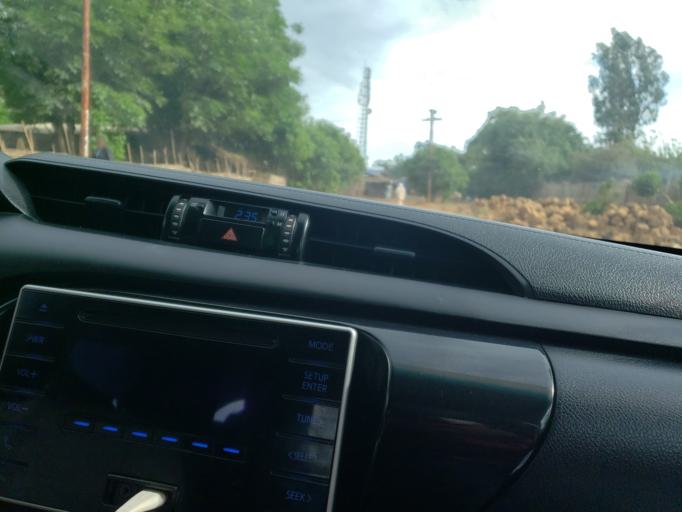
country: ET
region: Oromiya
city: Mendi
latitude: 10.2126
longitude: 35.0861
